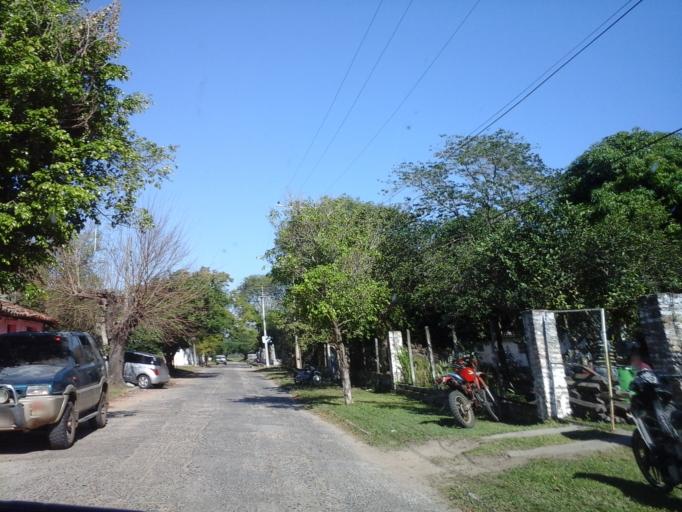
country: PY
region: Neembucu
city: Pilar
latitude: -26.8549
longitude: -58.3103
